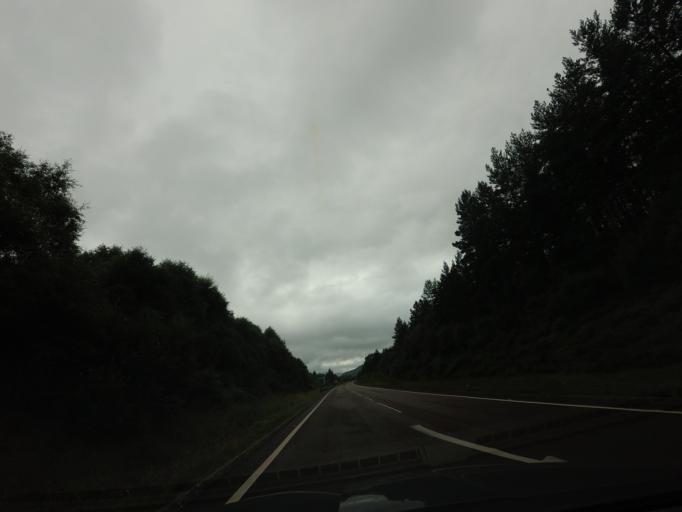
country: GB
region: Scotland
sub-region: Highland
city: Aviemore
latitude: 57.2203
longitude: -3.8210
